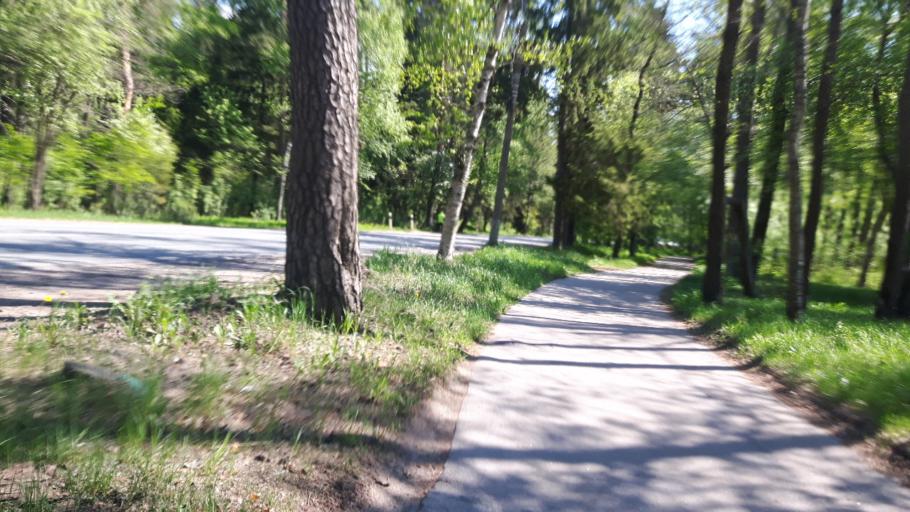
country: RU
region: St.-Petersburg
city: Komarovo
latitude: 60.1757
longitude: 29.7982
